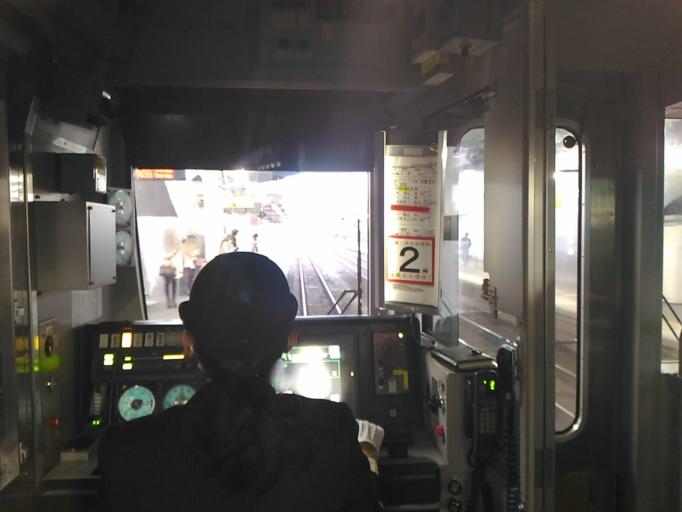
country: JP
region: Miyagi
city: Iwanuma
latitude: 38.1692
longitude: 140.8828
